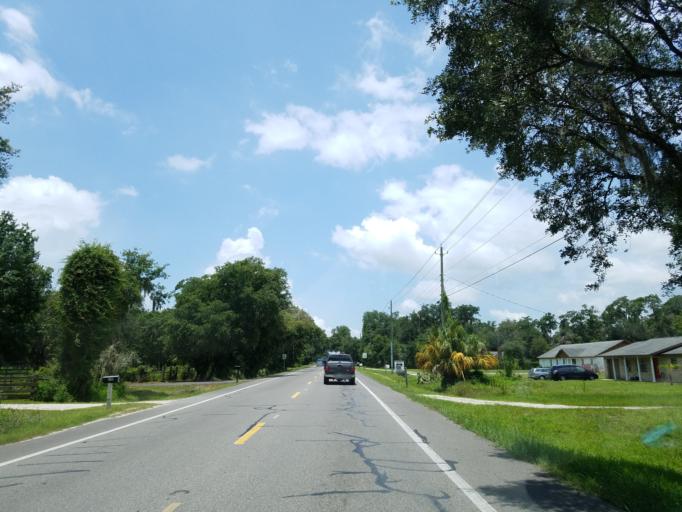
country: US
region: Florida
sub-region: Hillsborough County
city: Fish Hawk
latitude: 27.8505
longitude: -82.1408
